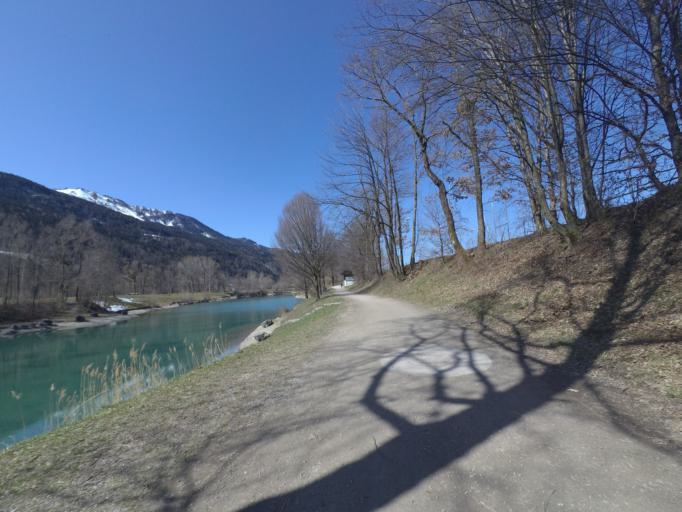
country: AT
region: Salzburg
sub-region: Politischer Bezirk Hallein
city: Kuchl
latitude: 47.6215
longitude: 13.1432
